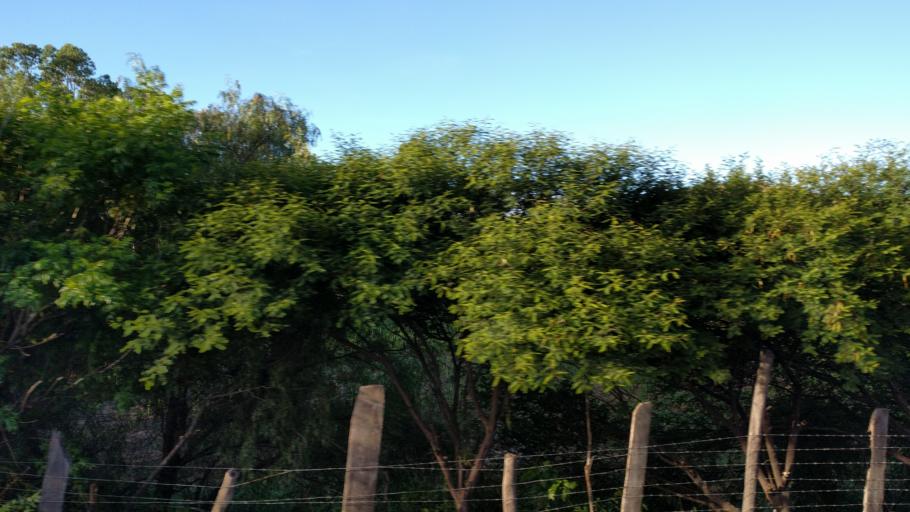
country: BO
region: Tarija
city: Tarija
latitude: -21.5188
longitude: -64.5724
